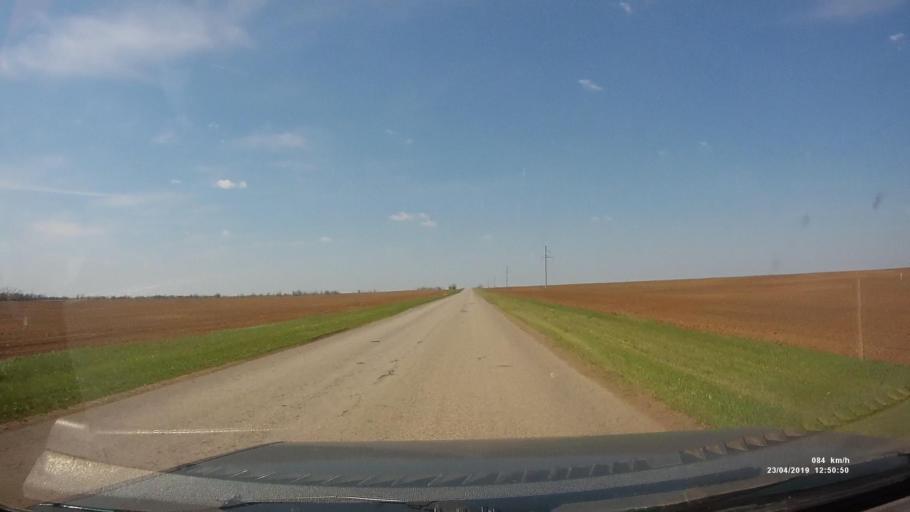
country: RU
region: Kalmykiya
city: Yashalta
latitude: 46.5491
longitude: 42.6306
